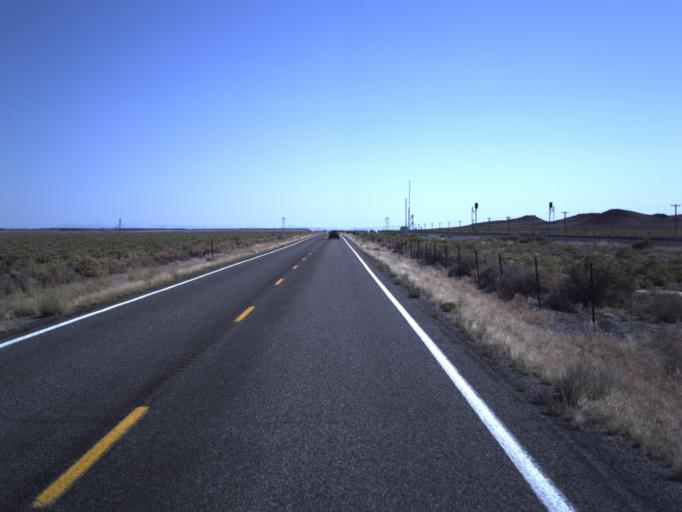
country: US
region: Utah
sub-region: Millard County
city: Delta
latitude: 39.1397
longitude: -112.7257
